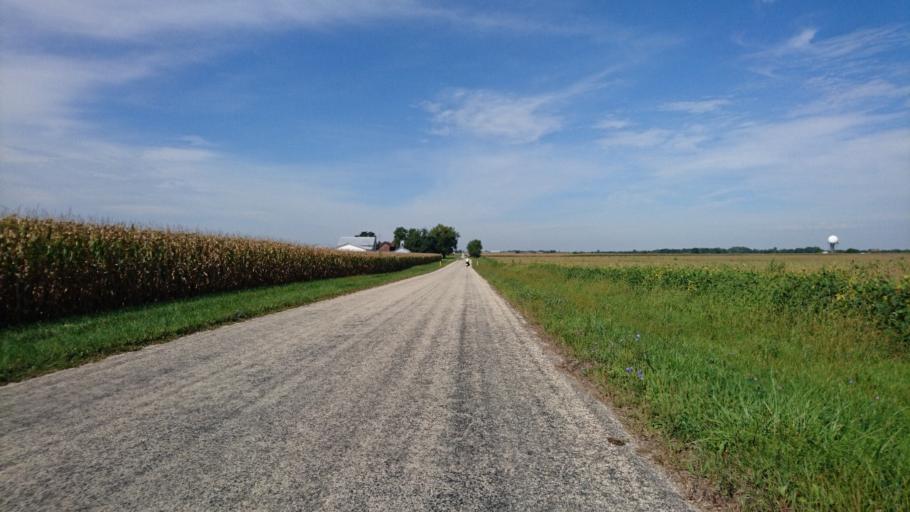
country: US
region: Illinois
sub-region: Will County
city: Manhattan
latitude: 41.4162
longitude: -88.0438
